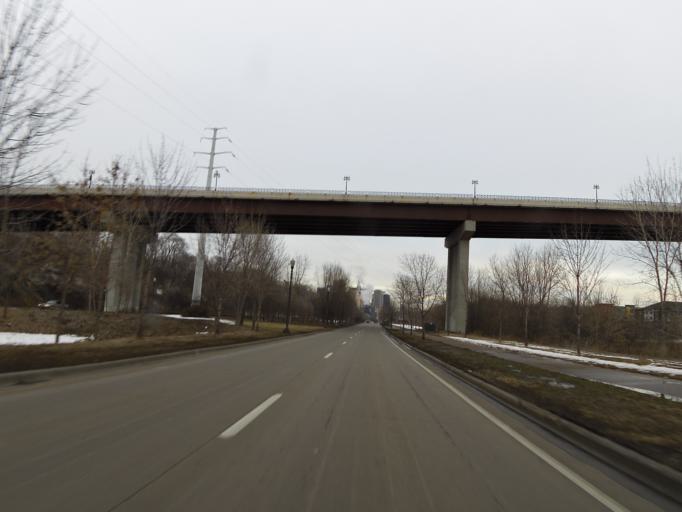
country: US
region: Minnesota
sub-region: Ramsey County
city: Saint Paul
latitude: 44.9355
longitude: -93.1092
